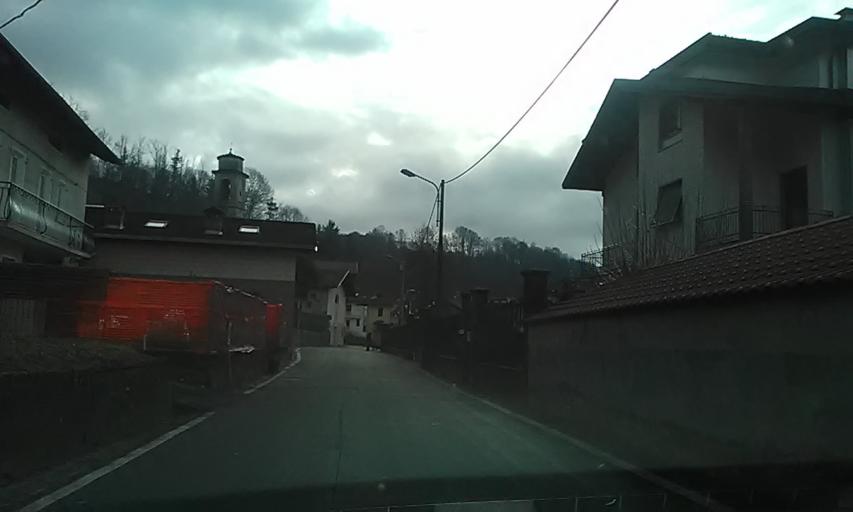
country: IT
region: Piedmont
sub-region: Provincia di Vercelli
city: Borgosesia
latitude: 45.7315
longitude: 8.2854
